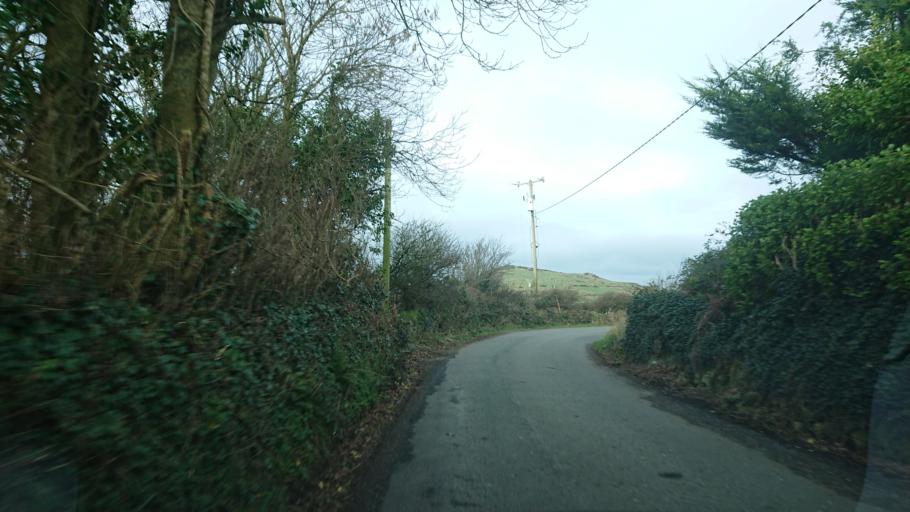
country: IE
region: Munster
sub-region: Waterford
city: Tra Mhor
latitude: 52.1596
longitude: -7.2149
